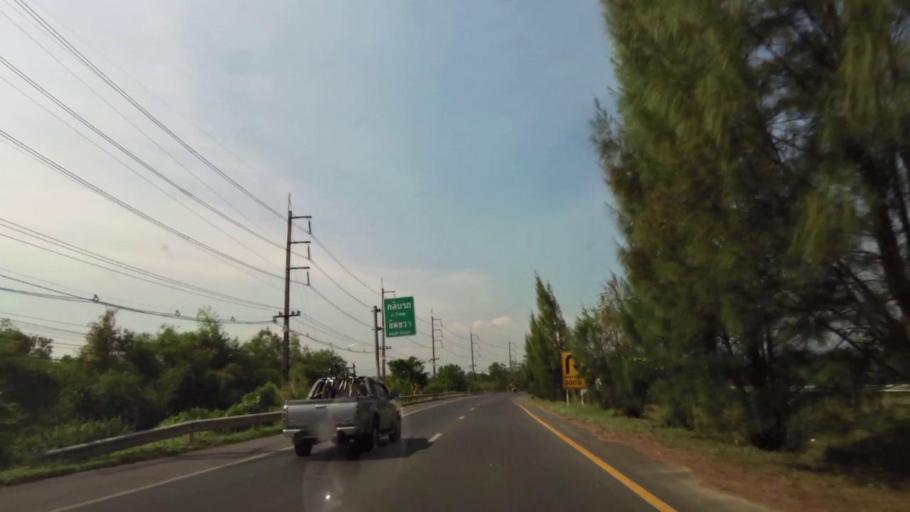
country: TH
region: Chanthaburi
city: Chanthaburi
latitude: 12.6416
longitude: 102.1321
